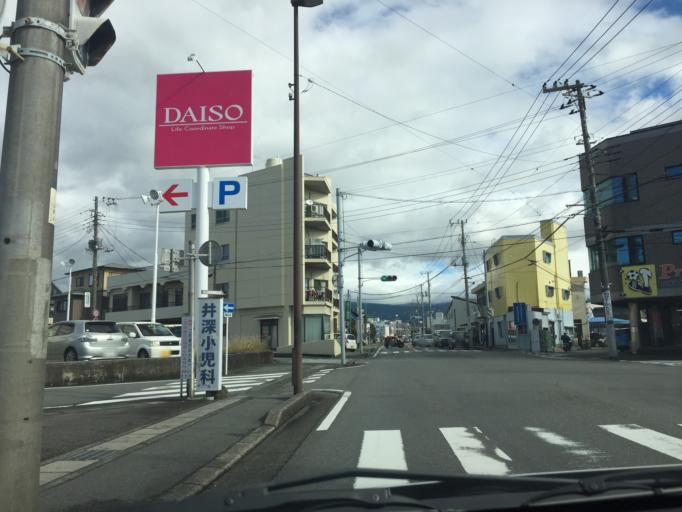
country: JP
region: Shizuoka
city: Mishima
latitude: 35.1162
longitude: 138.9026
